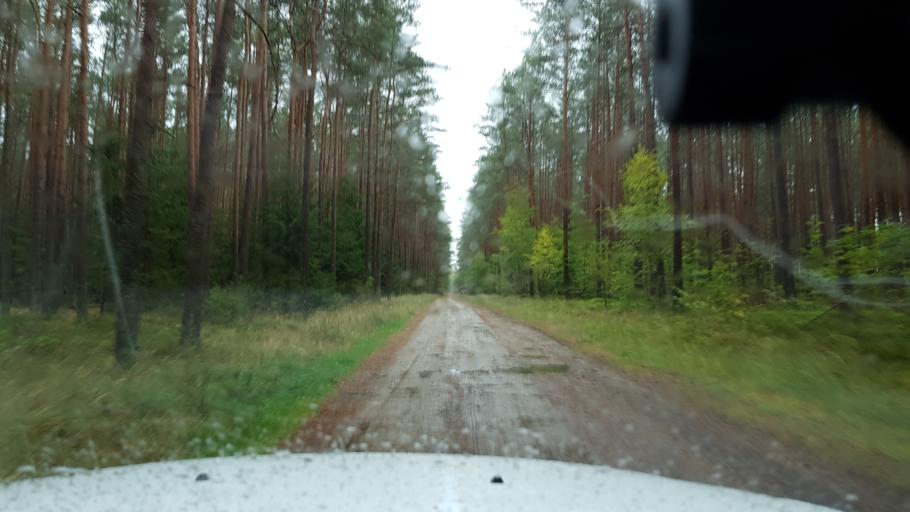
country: PL
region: West Pomeranian Voivodeship
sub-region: Powiat goleniowski
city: Przybiernow
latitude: 53.7291
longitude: 14.8086
